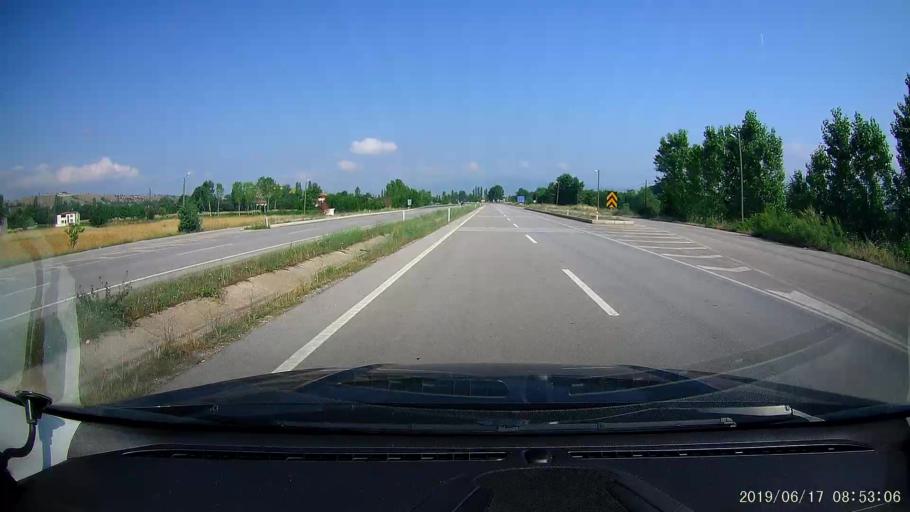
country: TR
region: Tokat
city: Erbaa
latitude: 40.7061
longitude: 36.4866
